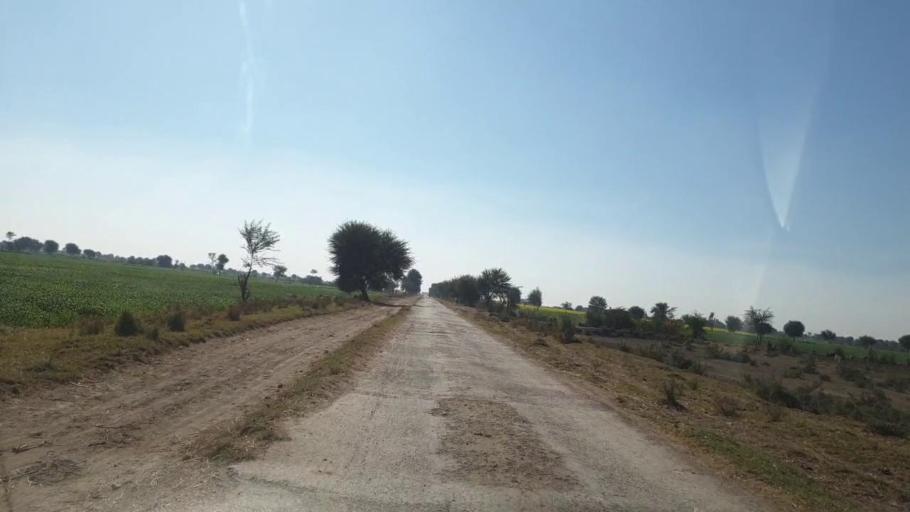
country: PK
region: Sindh
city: Jhol
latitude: 25.8172
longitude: 69.0358
